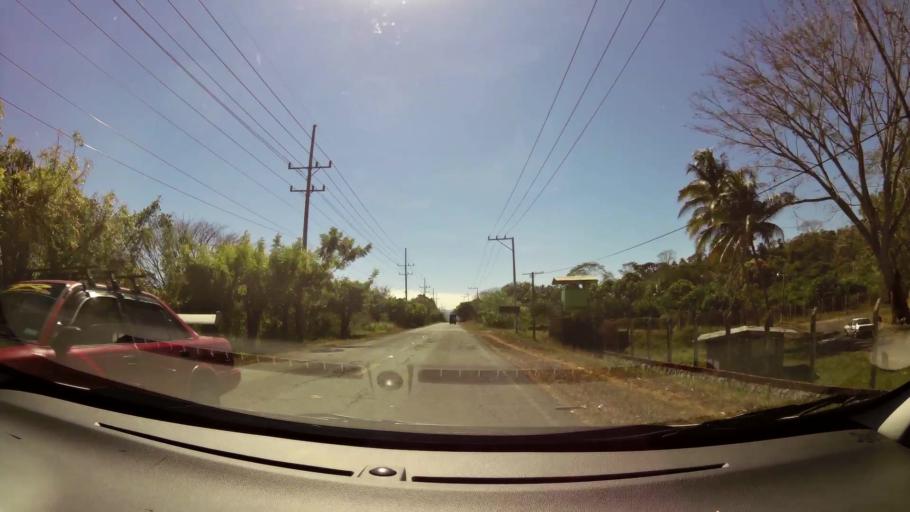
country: SV
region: La Libertad
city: San Juan Opico
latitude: 13.8370
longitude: -89.3594
